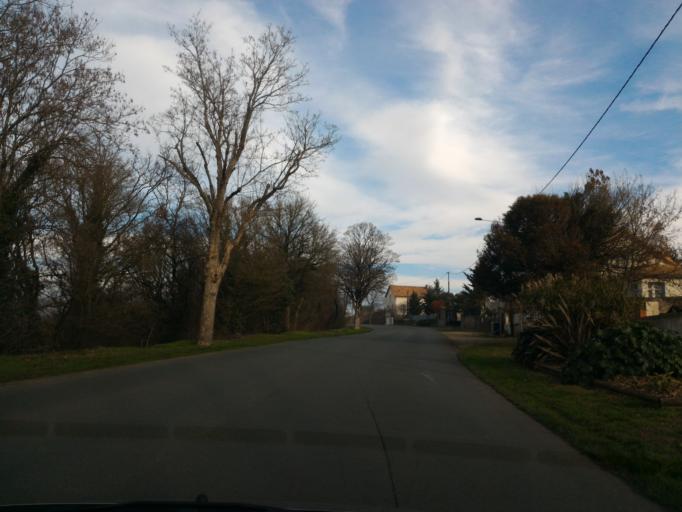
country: FR
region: Poitou-Charentes
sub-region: Departement de la Charente
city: Ruffec
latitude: 46.0345
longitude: 0.1963
